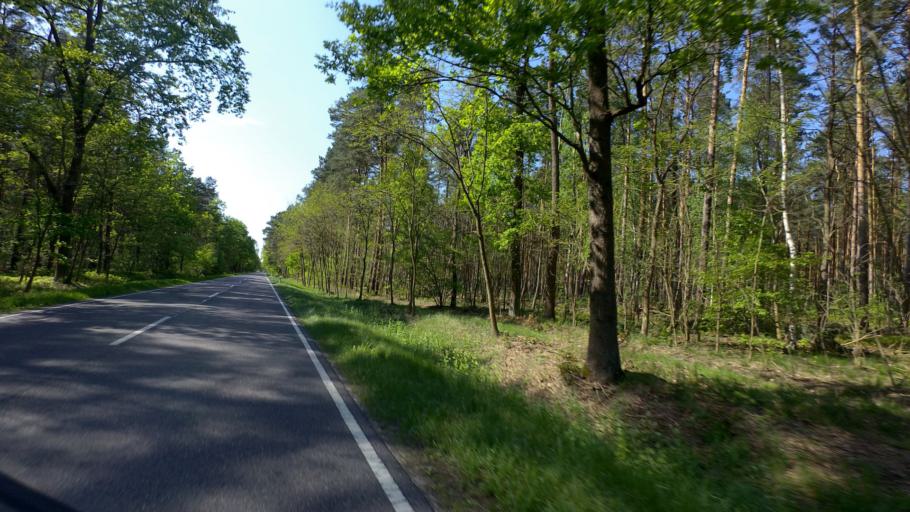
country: DE
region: Brandenburg
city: Schlepzig
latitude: 52.0665
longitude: 13.9125
